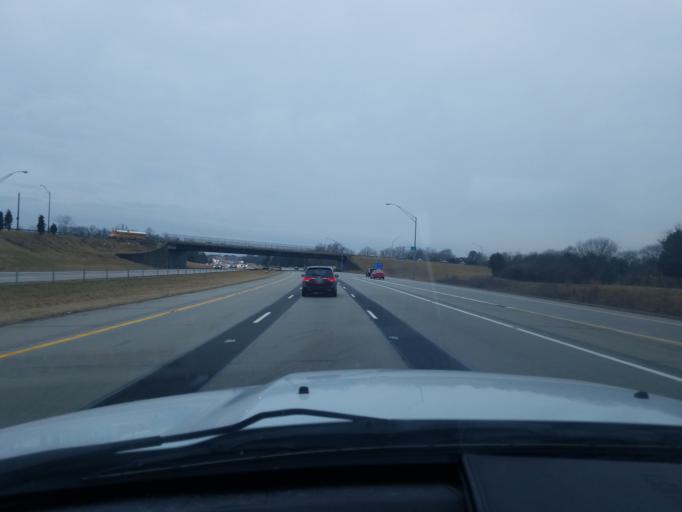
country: US
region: Ohio
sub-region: Montgomery County
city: Centerville
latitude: 39.6453
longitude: -84.1608
